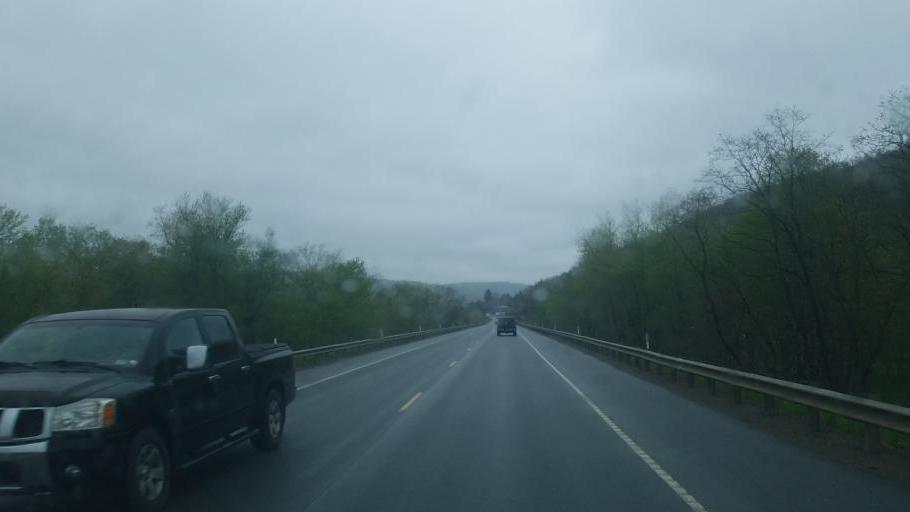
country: US
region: Pennsylvania
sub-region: McKean County
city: Port Allegany
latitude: 41.8008
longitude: -78.2648
